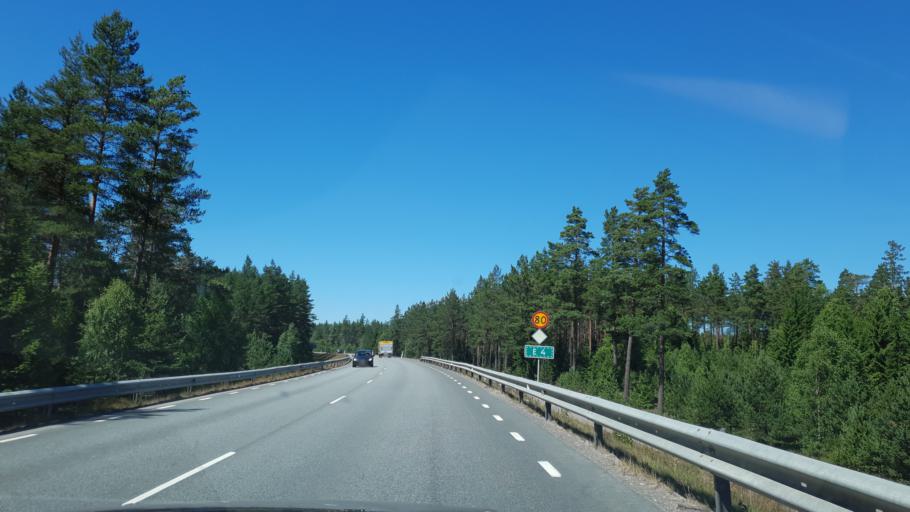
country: SE
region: Joenkoeping
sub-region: Vaggeryds Kommun
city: Vaggeryd
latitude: 57.5231
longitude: 14.1350
